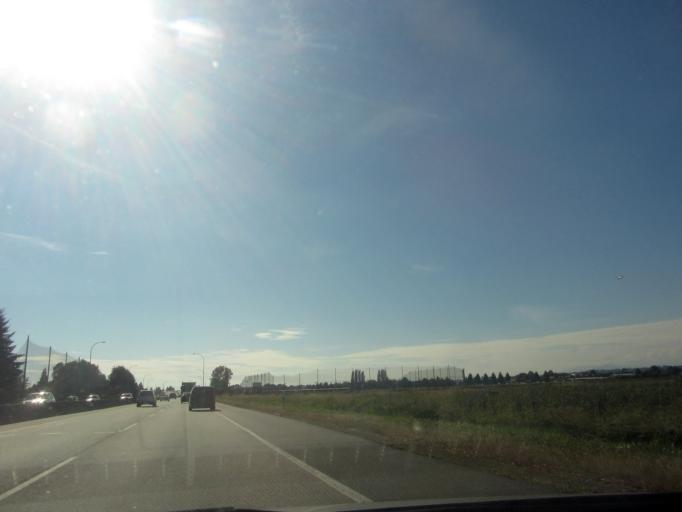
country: CA
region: British Columbia
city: Richmond
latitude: 49.1778
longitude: -123.0589
